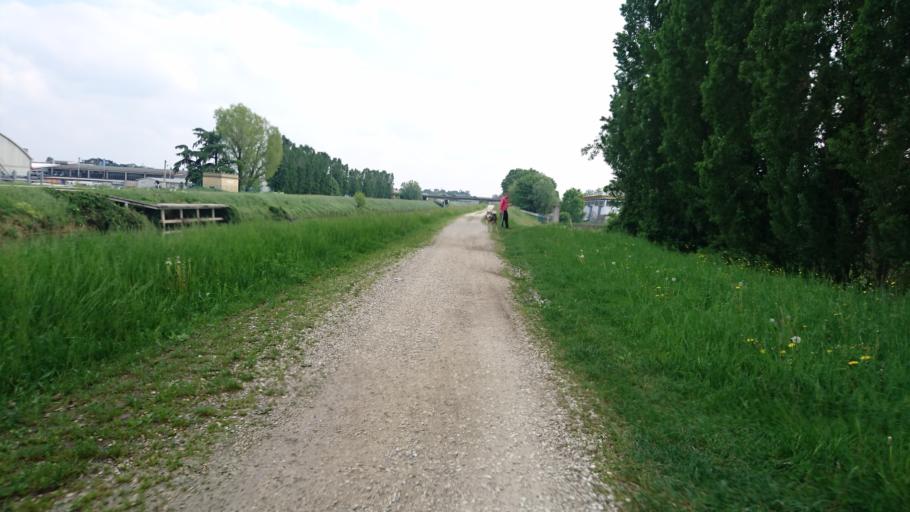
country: IT
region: Veneto
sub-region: Provincia di Padova
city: Noventa
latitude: 45.4065
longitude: 11.9274
